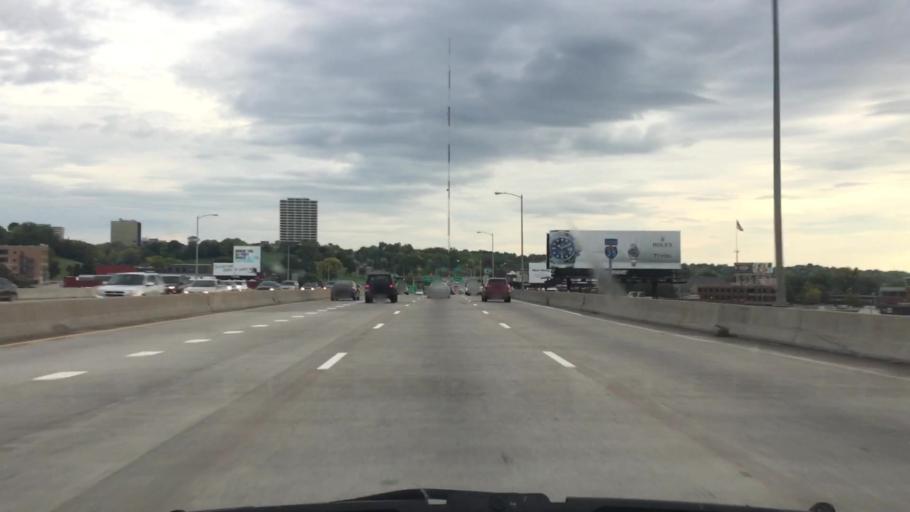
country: US
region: Missouri
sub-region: Jackson County
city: Kansas City
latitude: 39.0851
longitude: -94.5928
